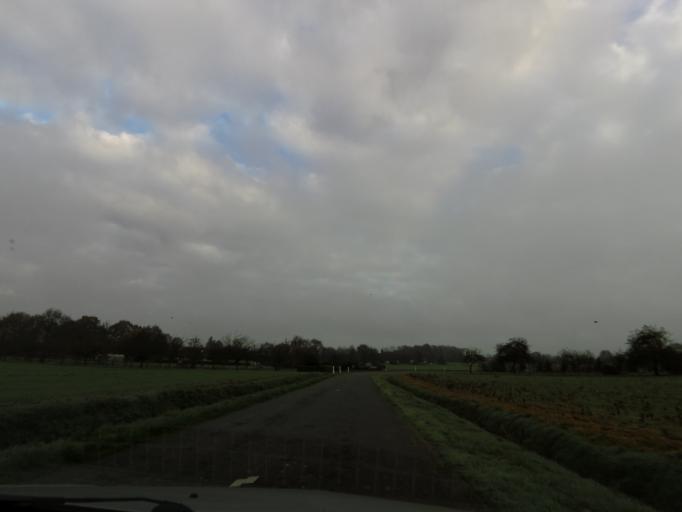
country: FR
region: Brittany
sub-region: Departement d'Ille-et-Vilaine
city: Chanteloup
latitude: 47.9554
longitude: -1.6401
